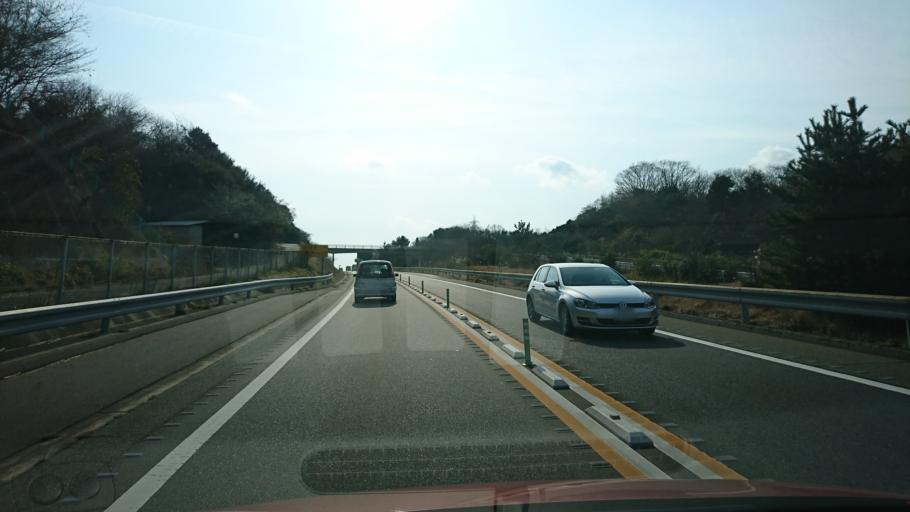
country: JP
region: Hiroshima
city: Onomichi
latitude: 34.3680
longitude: 133.1908
